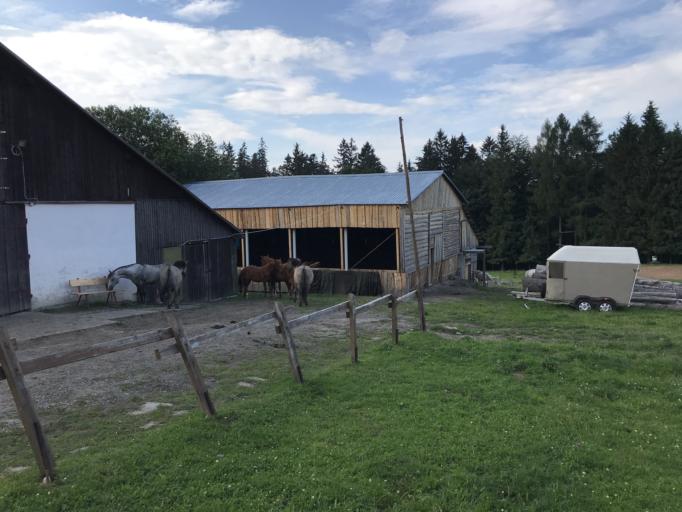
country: PL
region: Lower Silesian Voivodeship
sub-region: Powiat klodzki
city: Duszniki-Zdroj
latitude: 50.3707
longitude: 16.3809
